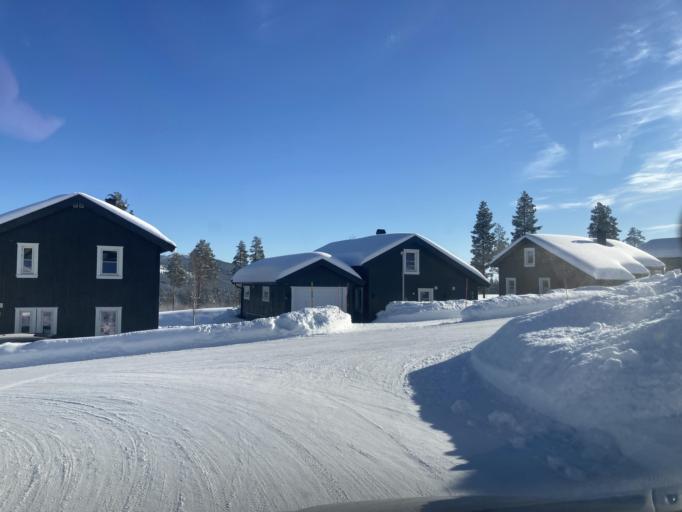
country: NO
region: Hedmark
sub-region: Trysil
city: Innbygda
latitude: 61.2983
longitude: 12.2417
